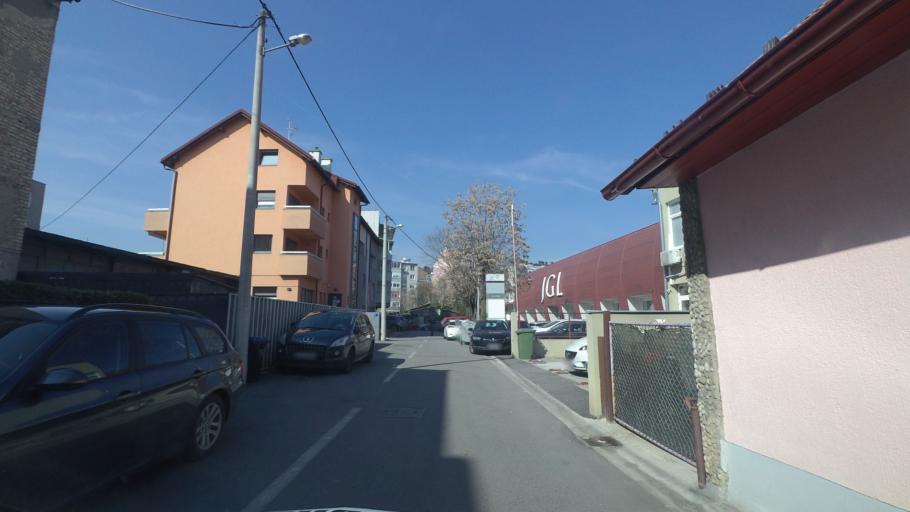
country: HR
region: Grad Zagreb
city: Zagreb - Centar
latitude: 45.8007
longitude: 15.9605
